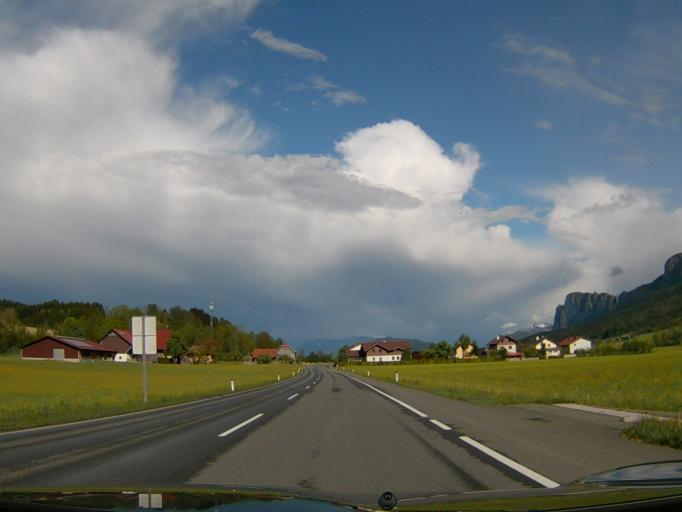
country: AT
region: Salzburg
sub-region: Politischer Bezirk Salzburg-Umgebung
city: Thalgau
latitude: 47.8431
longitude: 13.2608
